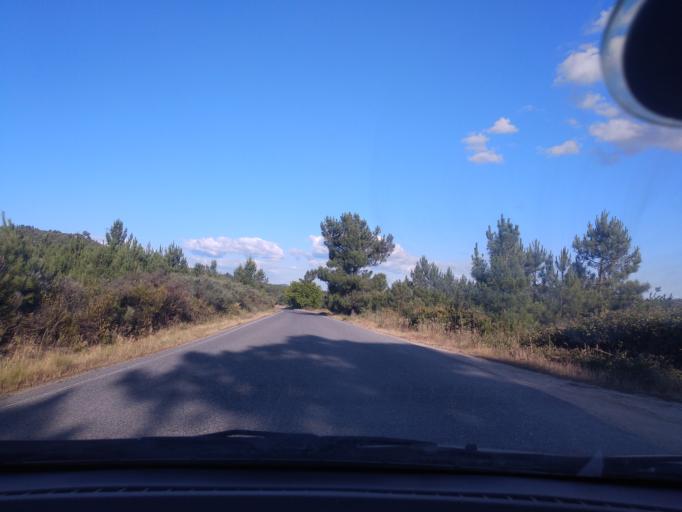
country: PT
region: Castelo Branco
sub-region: Covilha
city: Teixoso
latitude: 40.2350
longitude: -7.3805
